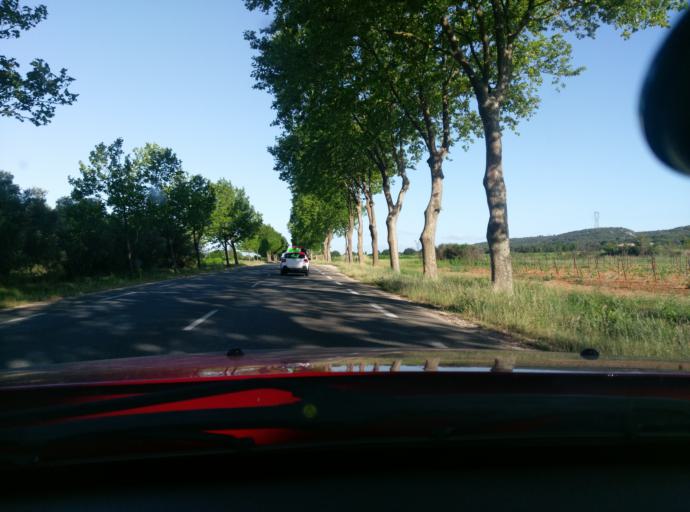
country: FR
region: Languedoc-Roussillon
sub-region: Departement du Gard
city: Castillon-du-Gard
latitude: 43.9758
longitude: 4.4864
